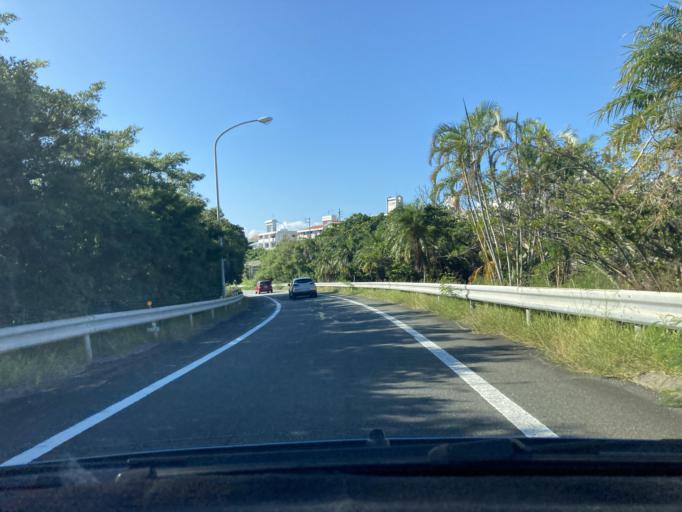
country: JP
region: Okinawa
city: Ginowan
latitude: 26.2488
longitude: 127.7466
